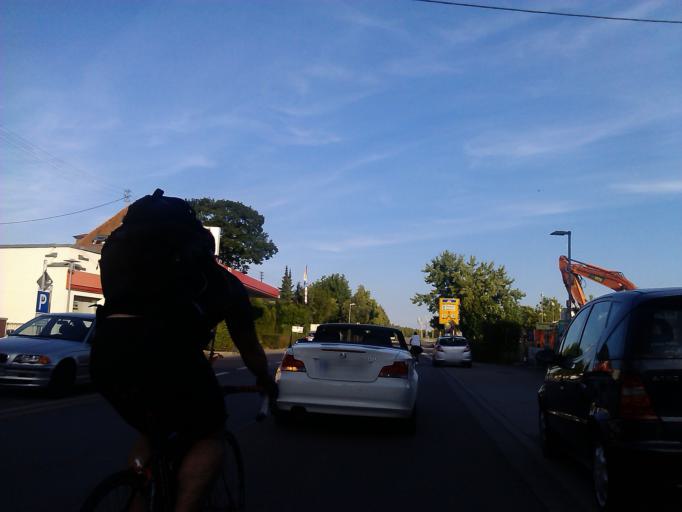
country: DE
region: Baden-Wuerttemberg
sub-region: Karlsruhe Region
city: Walldorf
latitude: 49.3006
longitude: 8.6444
